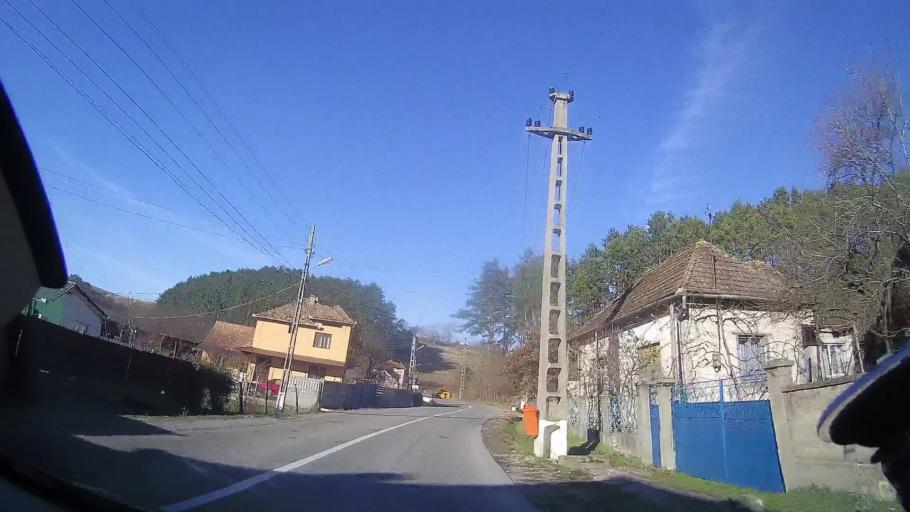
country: RO
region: Bihor
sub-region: Comuna Bratca
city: Bratca
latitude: 46.9295
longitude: 22.6019
